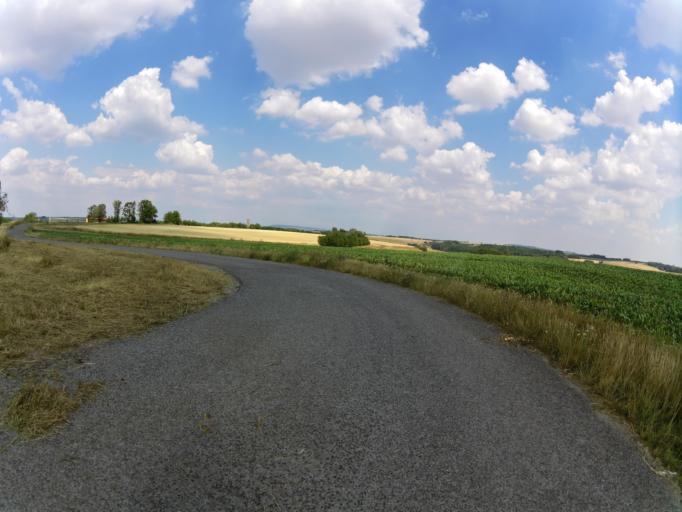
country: DE
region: Bavaria
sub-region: Regierungsbezirk Unterfranken
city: Ochsenfurt
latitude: 49.6475
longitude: 10.0698
